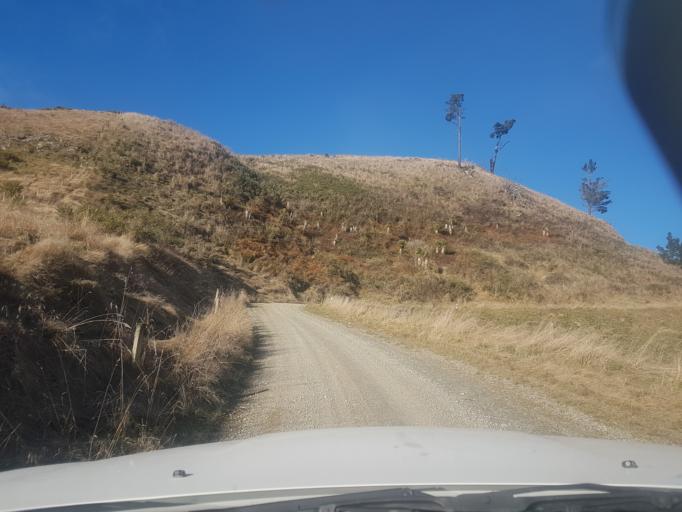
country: NZ
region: Canterbury
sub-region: Timaru District
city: Pleasant Point
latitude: -44.1665
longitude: 170.8802
